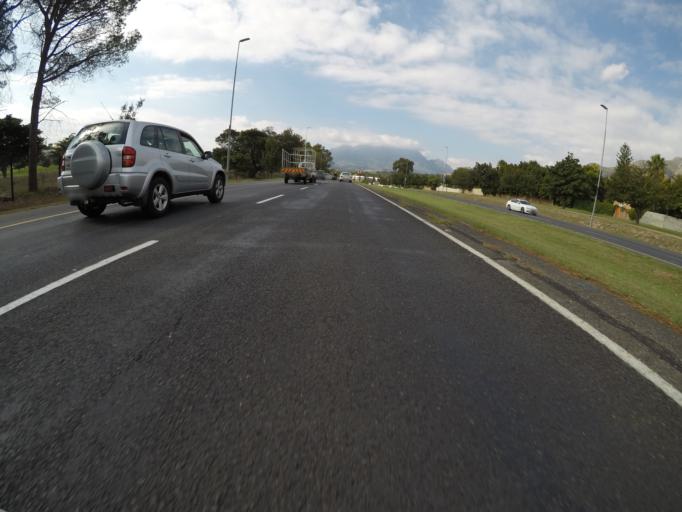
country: ZA
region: Western Cape
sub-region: Cape Winelands District Municipality
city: Stellenbosch
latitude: -33.9615
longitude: 18.8515
